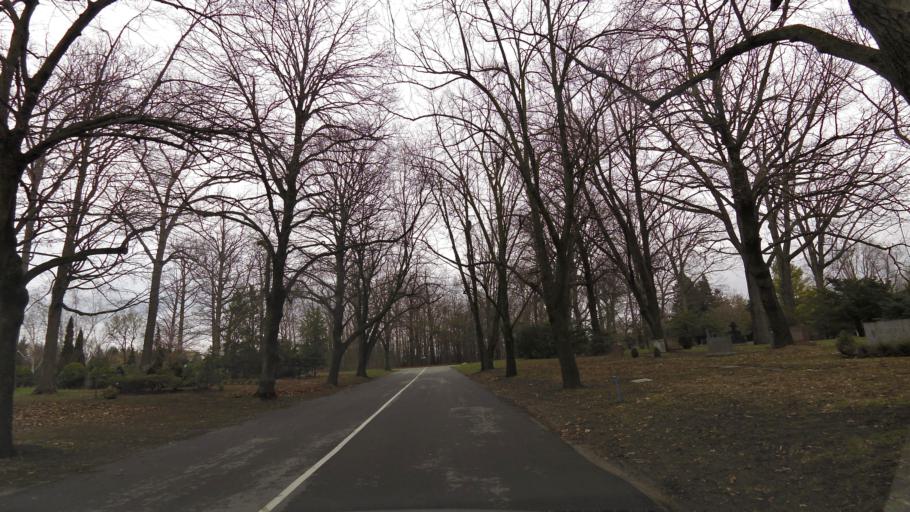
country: CA
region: Ontario
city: Toronto
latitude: 43.6978
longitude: -79.3797
